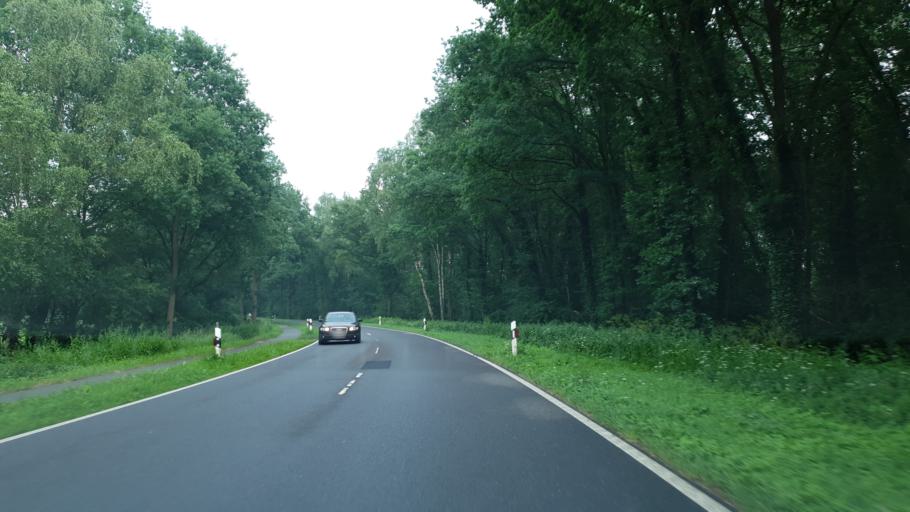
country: DE
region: Lower Saxony
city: Meppen
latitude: 52.6803
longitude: 7.3290
